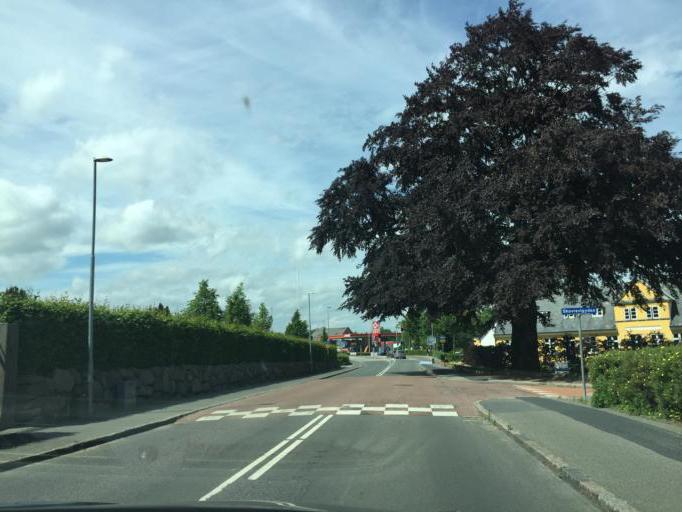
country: DK
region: South Denmark
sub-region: Odense Kommune
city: Hojby
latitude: 55.3036
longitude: 10.3971
